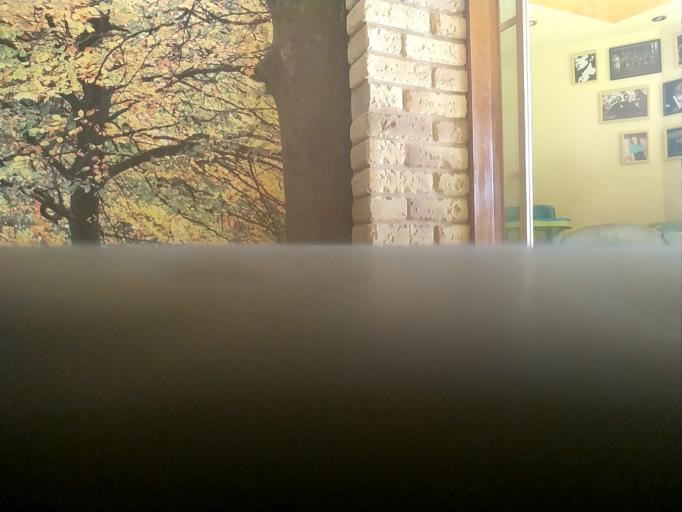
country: RU
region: Smolensk
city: Temkino
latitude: 55.1094
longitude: 34.8961
